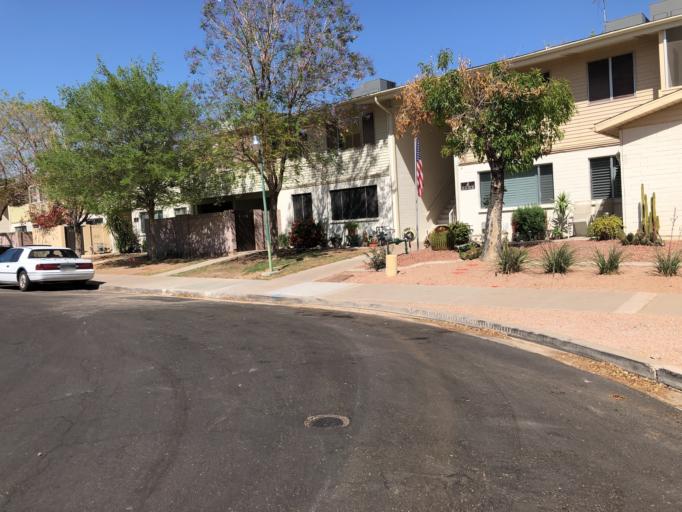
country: US
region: Arizona
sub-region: Maricopa County
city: Tempe
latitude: 33.4564
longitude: -111.9049
